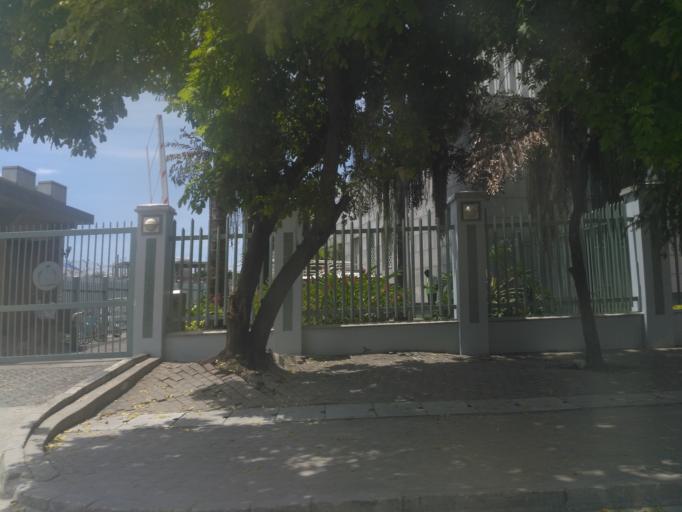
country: TZ
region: Zanzibar Urban/West
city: Zanzibar
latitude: -6.1581
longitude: 39.2041
